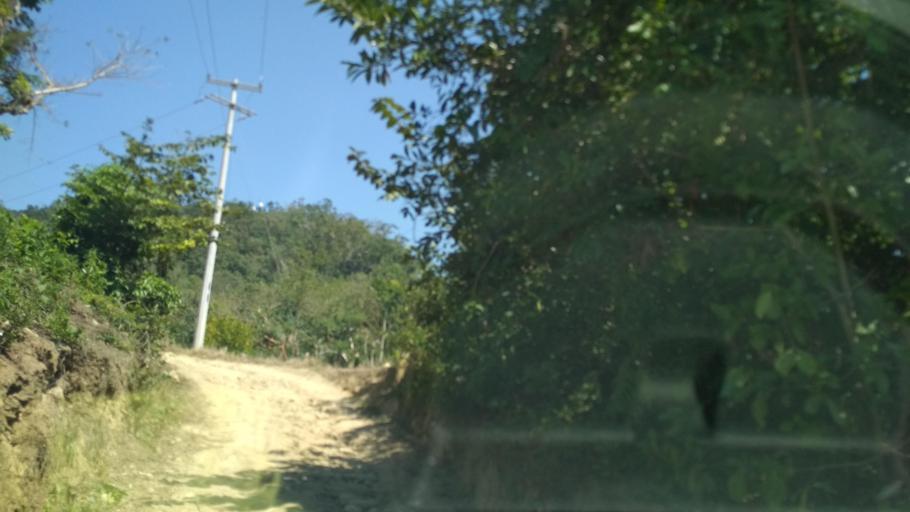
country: MX
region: Veracruz
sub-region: Papantla
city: Polutla
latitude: 20.4837
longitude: -97.2271
